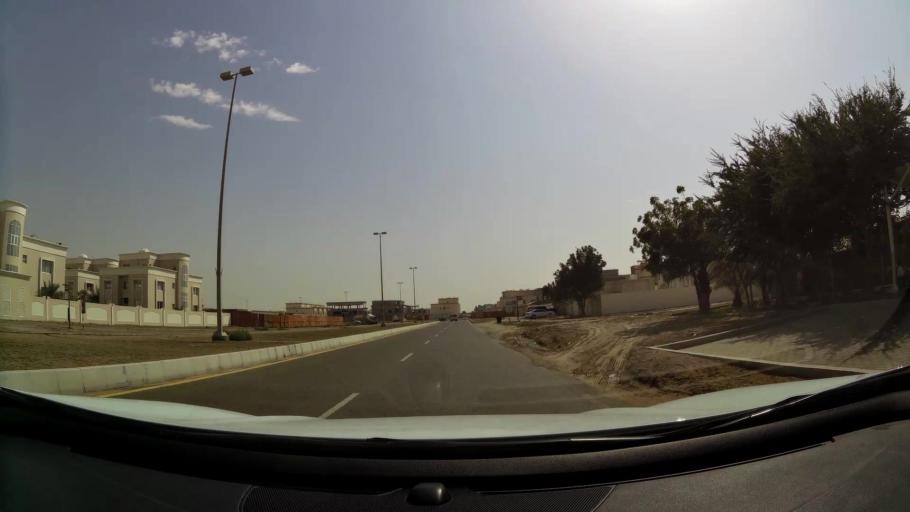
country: AE
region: Abu Dhabi
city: Abu Dhabi
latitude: 24.3342
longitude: 54.5487
